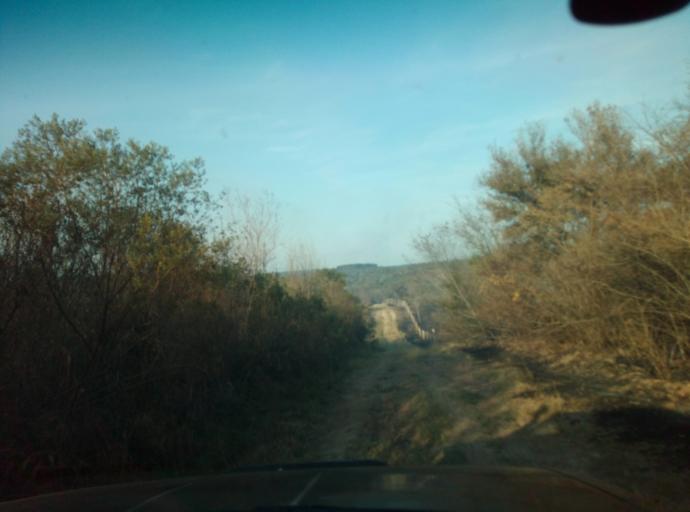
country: PY
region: Caaguazu
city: Doctor Cecilio Baez
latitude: -25.1996
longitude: -56.1169
